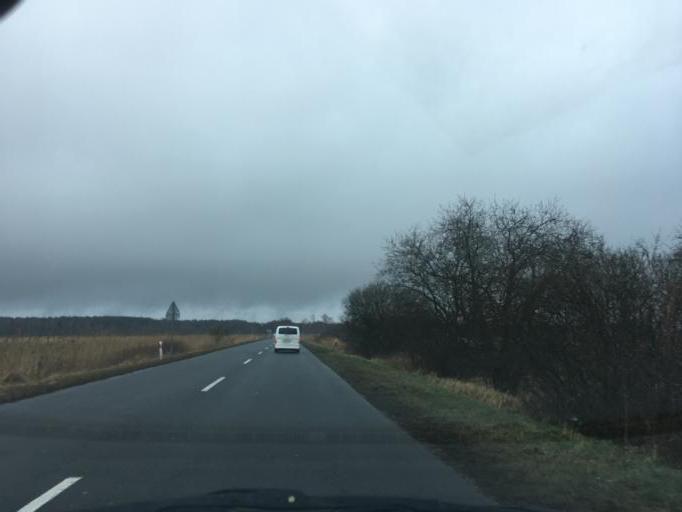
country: PL
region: West Pomeranian Voivodeship
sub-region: Swinoujscie
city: Swinoujscie
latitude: 53.8689
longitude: 14.2994
